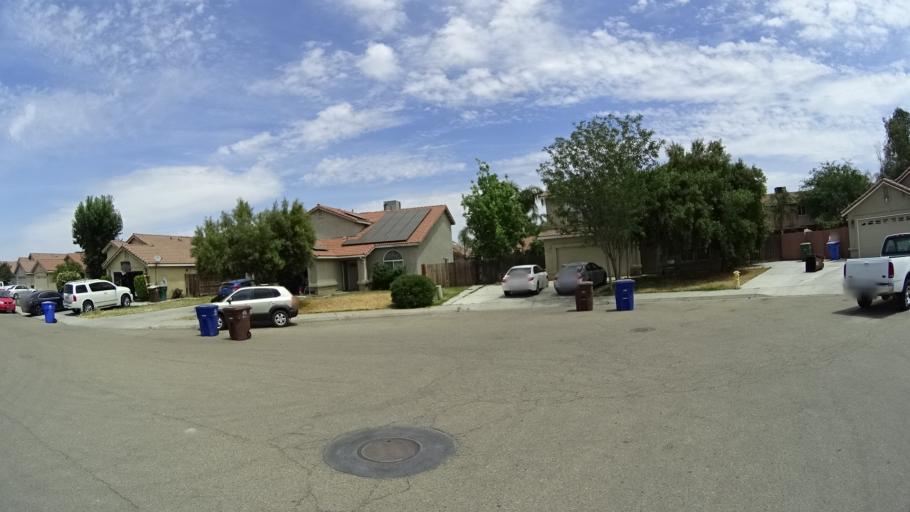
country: US
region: California
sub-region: Kings County
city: Armona
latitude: 36.3181
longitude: -119.7025
